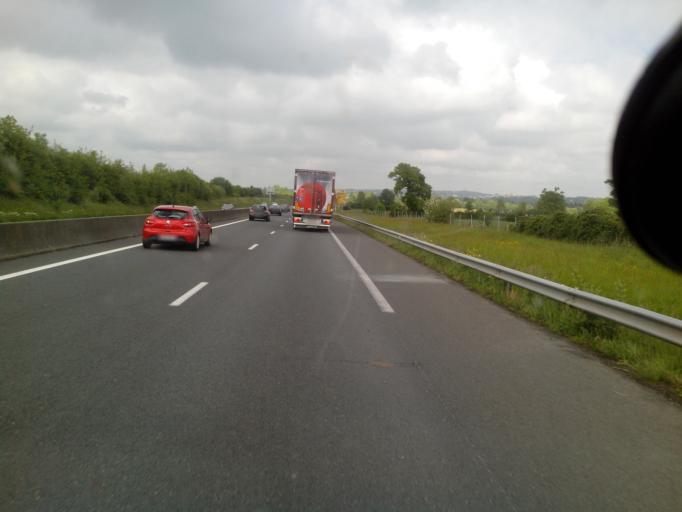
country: FR
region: Lower Normandy
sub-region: Departement du Calvados
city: Villers-Bocage
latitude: 49.0557
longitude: -0.7002
